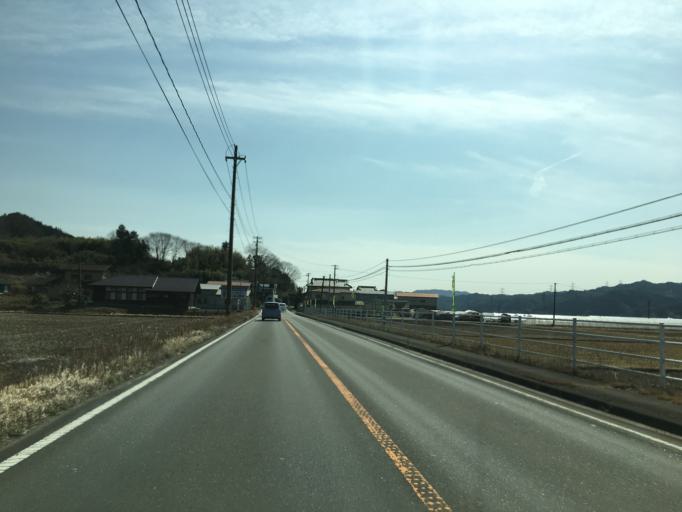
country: JP
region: Ibaraki
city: Daigo
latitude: 36.9180
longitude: 140.4165
